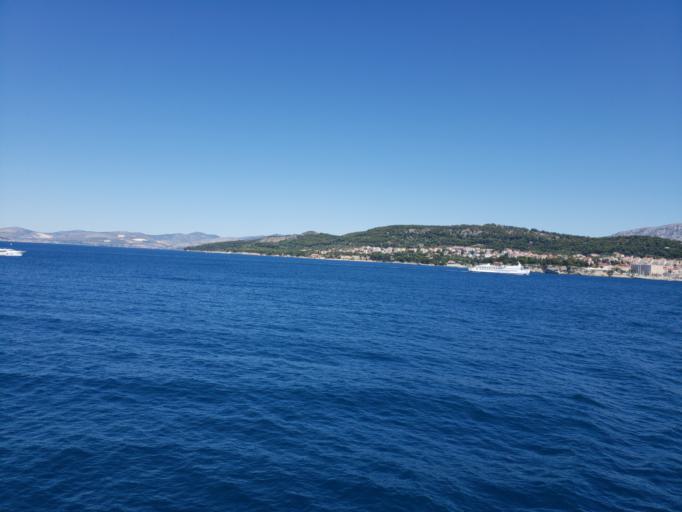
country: HR
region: Splitsko-Dalmatinska
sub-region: Grad Split
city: Split
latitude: 43.4911
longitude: 16.4329
